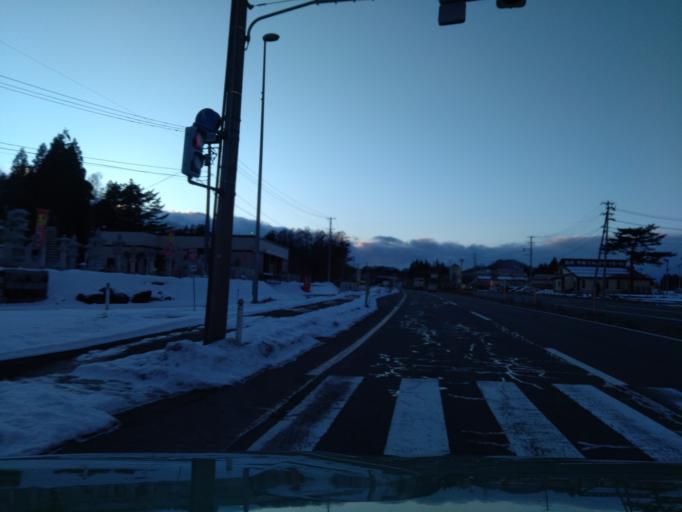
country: JP
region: Iwate
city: Shizukuishi
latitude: 39.7021
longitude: 141.0355
